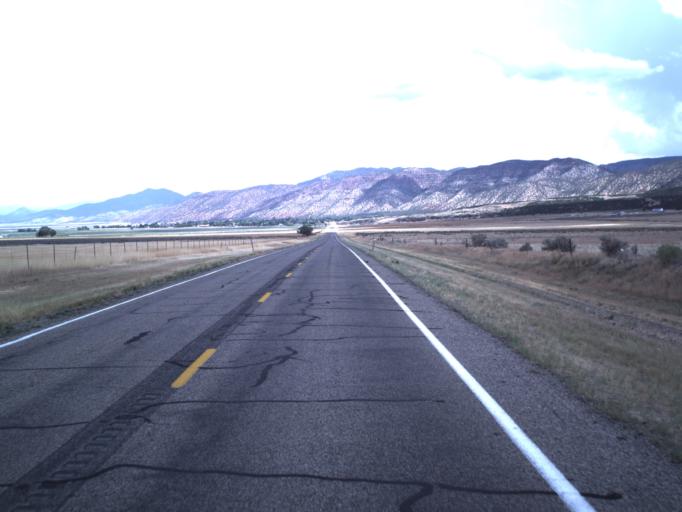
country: US
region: Utah
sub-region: Iron County
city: Parowan
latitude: 37.8610
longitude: -112.8107
